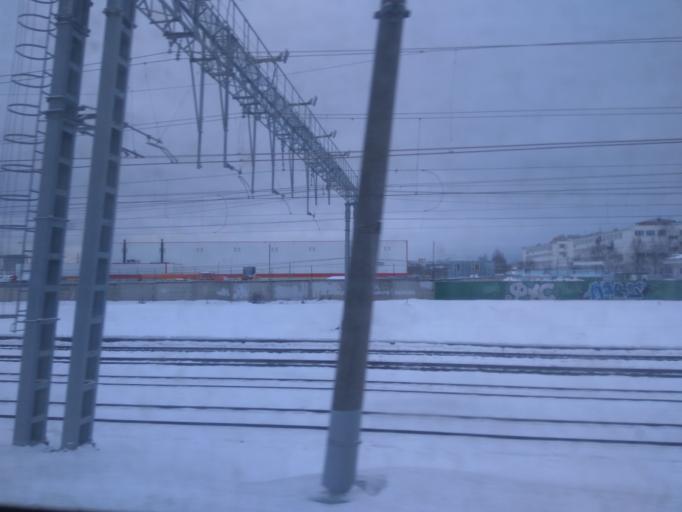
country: RU
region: Moskovskaya
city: Shcherbinka
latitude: 55.4831
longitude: 37.5544
